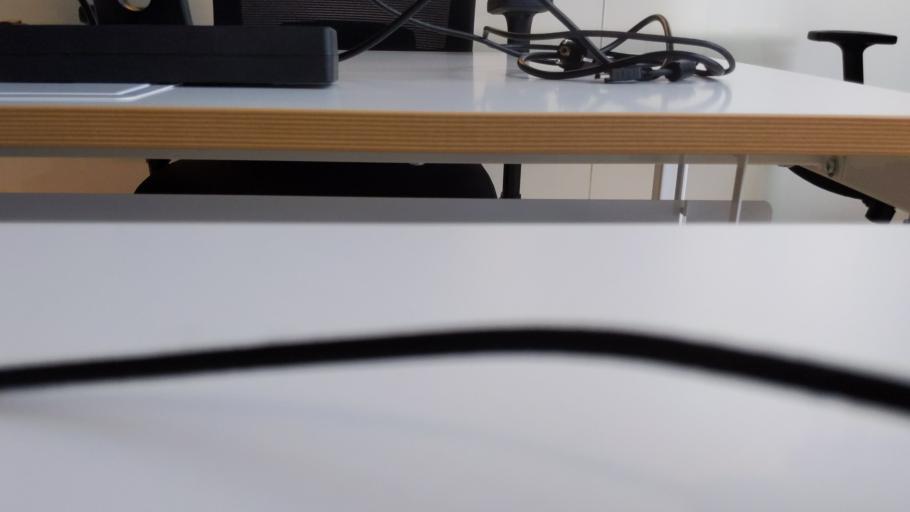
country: RU
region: Moskovskaya
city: Shevlyakovo
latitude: 56.4064
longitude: 36.8865
